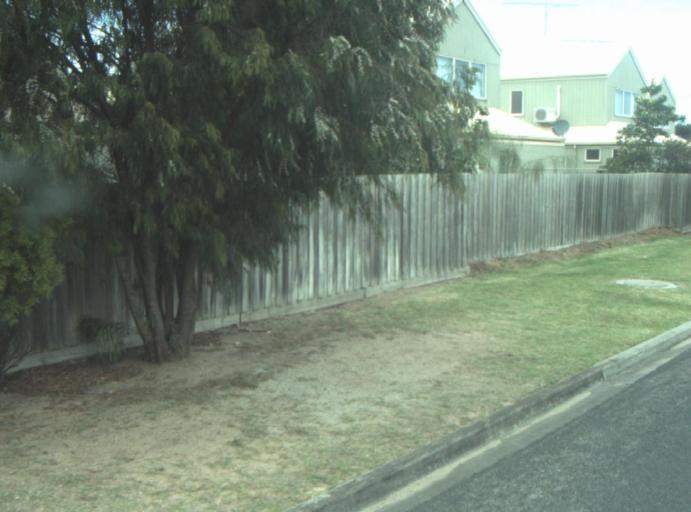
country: AU
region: Victoria
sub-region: Greater Geelong
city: Leopold
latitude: -38.2679
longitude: 144.5145
